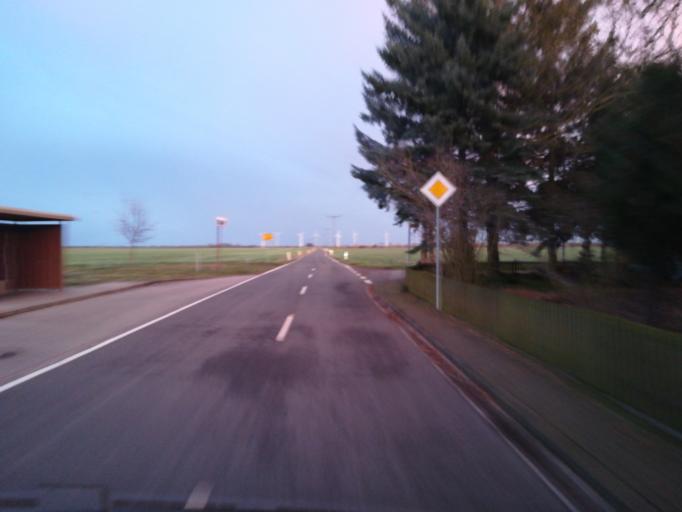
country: DE
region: Saxony-Anhalt
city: Roitzsch
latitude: 51.5559
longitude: 12.2483
